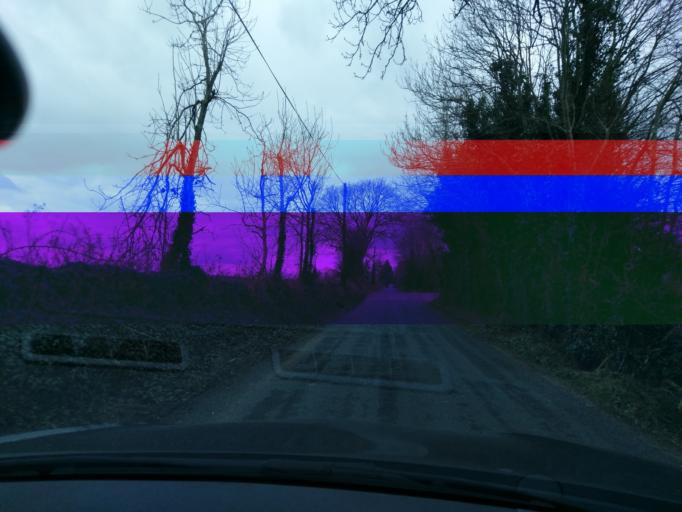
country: IE
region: Connaught
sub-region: County Galway
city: Athenry
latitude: 53.4546
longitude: -8.5842
